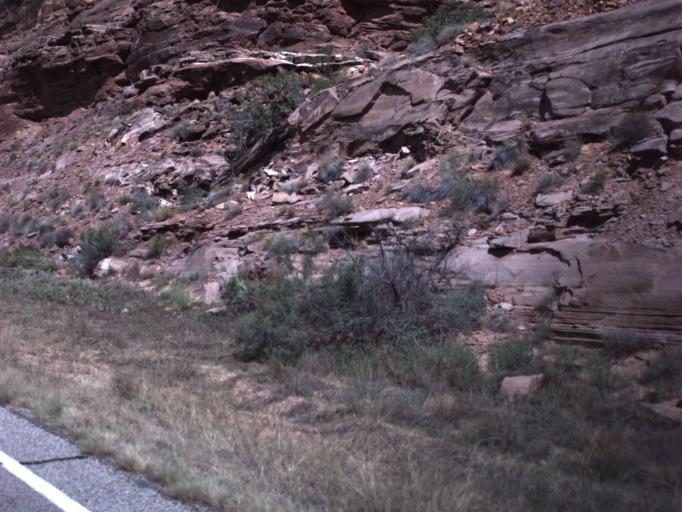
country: US
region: Utah
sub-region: Grand County
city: Moab
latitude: 38.5485
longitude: -109.6315
